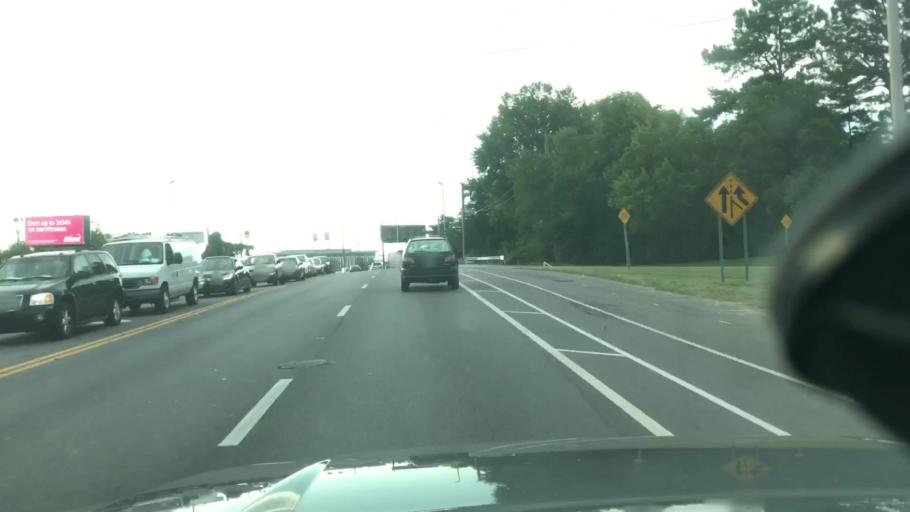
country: US
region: Tennessee
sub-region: Davidson County
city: Oak Hill
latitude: 36.1180
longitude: -86.7001
